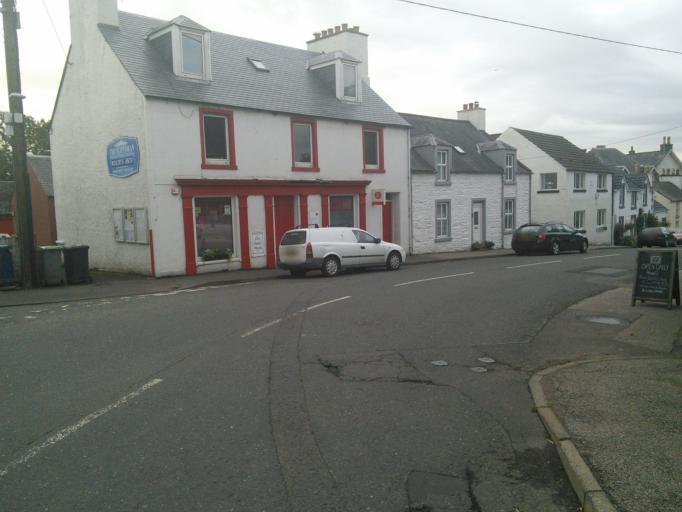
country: GB
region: Scotland
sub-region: Dumfries and Galloway
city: Castle Douglas
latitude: 55.1058
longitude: -4.1651
